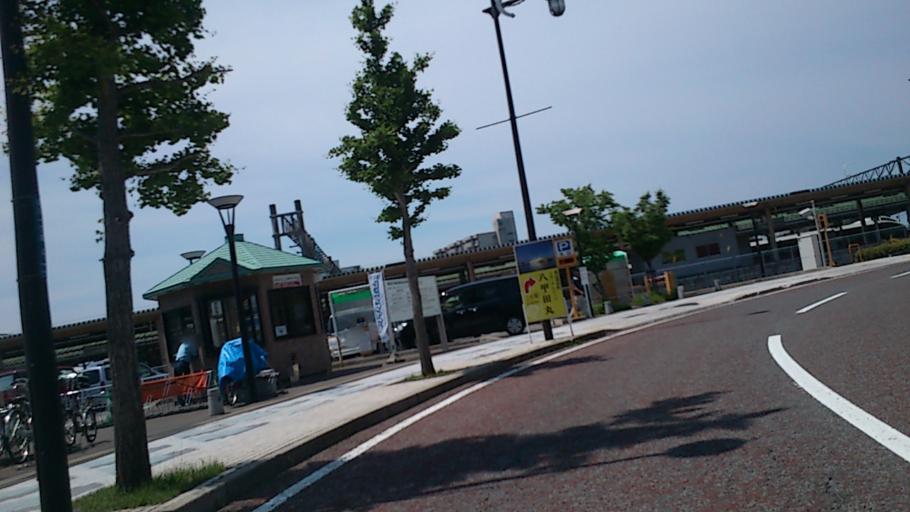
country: JP
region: Aomori
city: Aomori Shi
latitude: 40.8294
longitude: 140.7352
